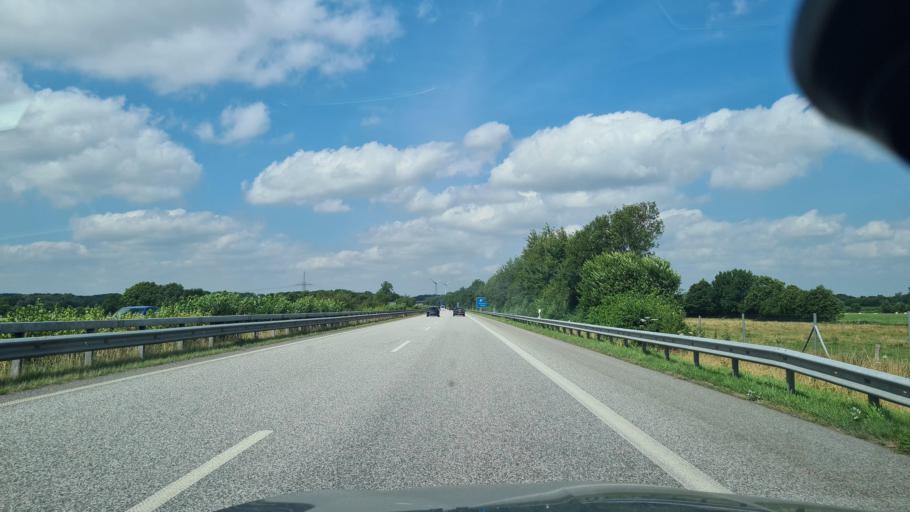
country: DE
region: Schleswig-Holstein
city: Hadenfeld
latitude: 54.0225
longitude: 9.4575
